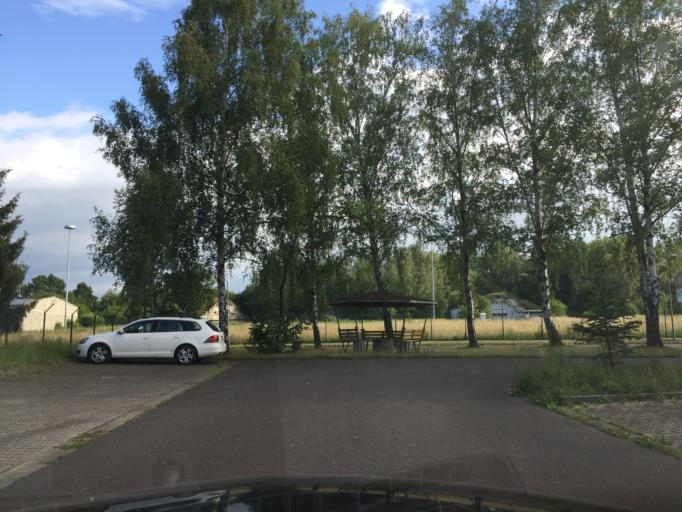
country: DE
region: Thuringia
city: Nobitz
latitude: 50.9816
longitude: 12.5160
